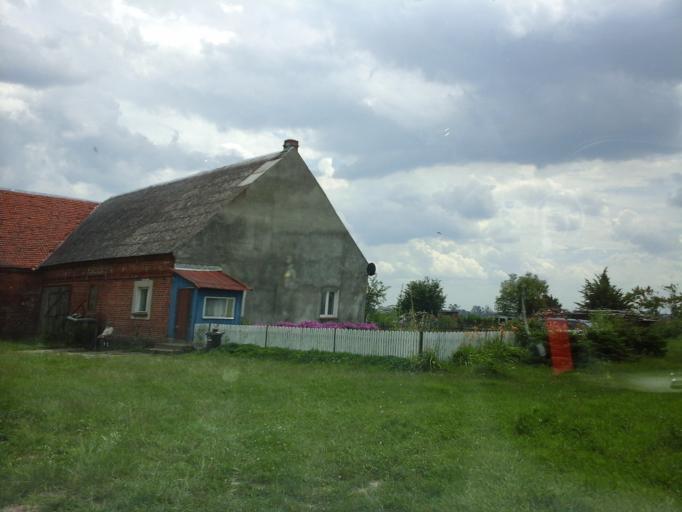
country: PL
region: West Pomeranian Voivodeship
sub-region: Powiat choszczenski
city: Bierzwnik
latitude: 53.0448
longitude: 15.7093
